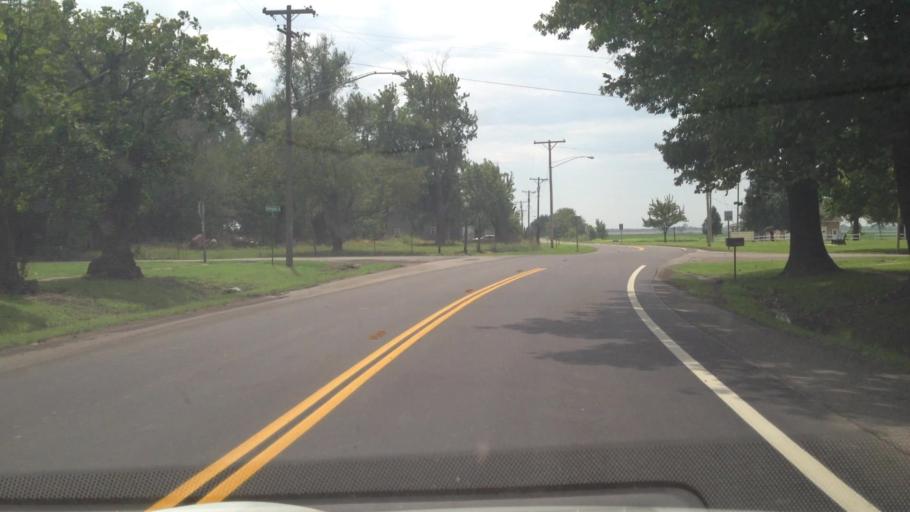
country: US
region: Kansas
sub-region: Crawford County
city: Girard
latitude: 37.6605
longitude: -94.9696
